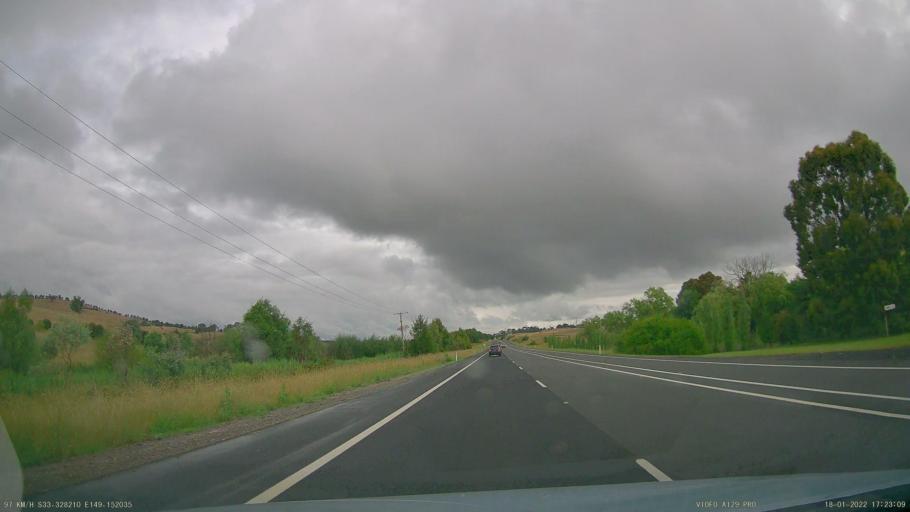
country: AU
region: New South Wales
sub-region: Orange Municipality
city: Orange
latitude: -33.3284
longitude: 149.1521
